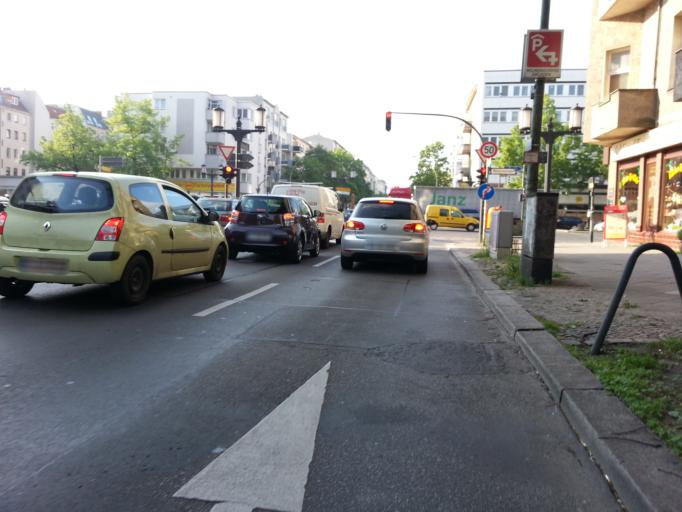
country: DE
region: Berlin
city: Charlottenburg Bezirk
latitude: 52.5117
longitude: 13.3013
